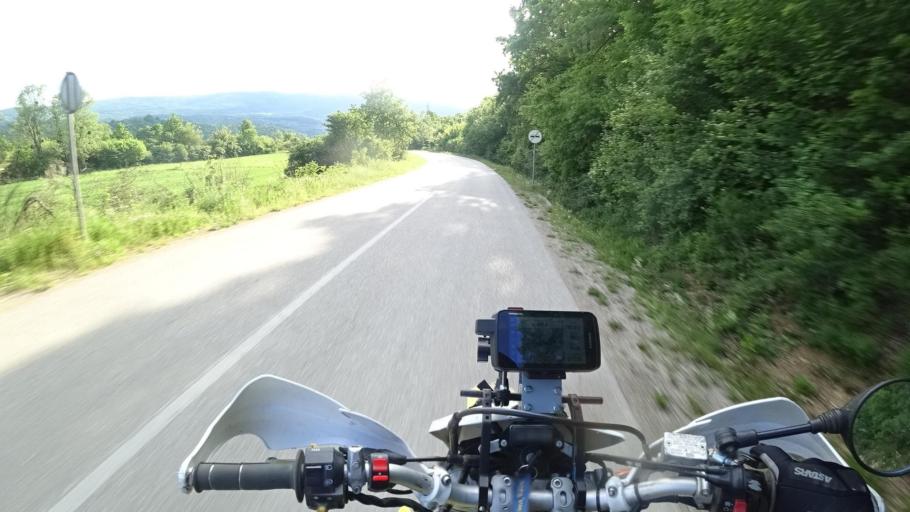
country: BA
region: Federation of Bosnia and Herzegovina
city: Sanica
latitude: 44.6191
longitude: 16.6677
